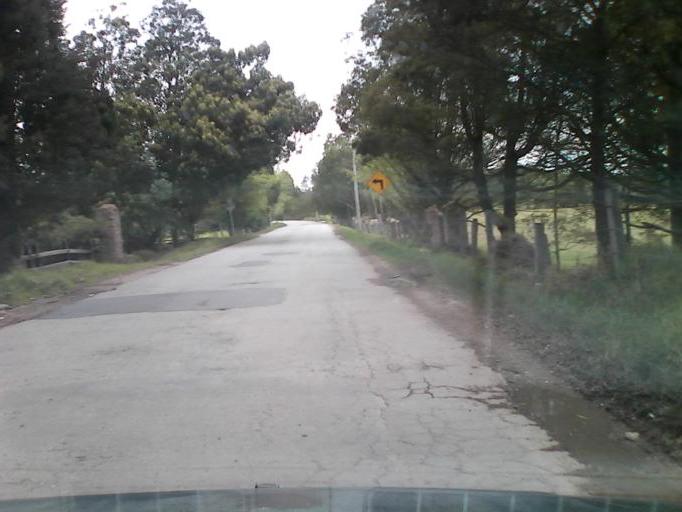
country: CO
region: Boyaca
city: Duitama
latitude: 5.7864
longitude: -73.0506
